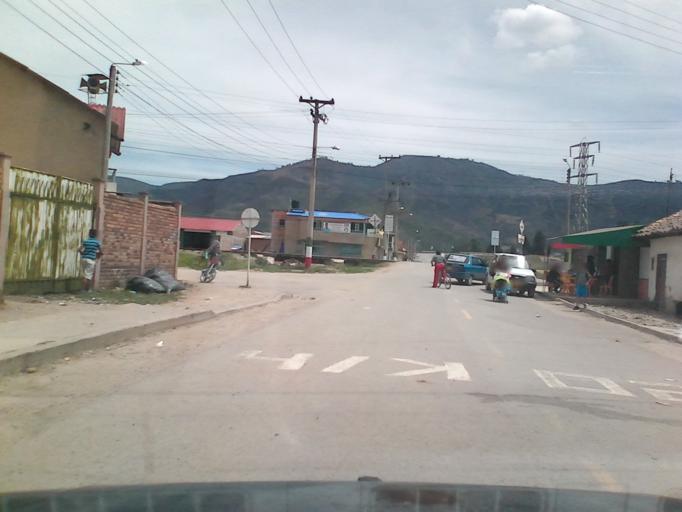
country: CO
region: Boyaca
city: Tibasosa
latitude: 5.7925
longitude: -72.9925
